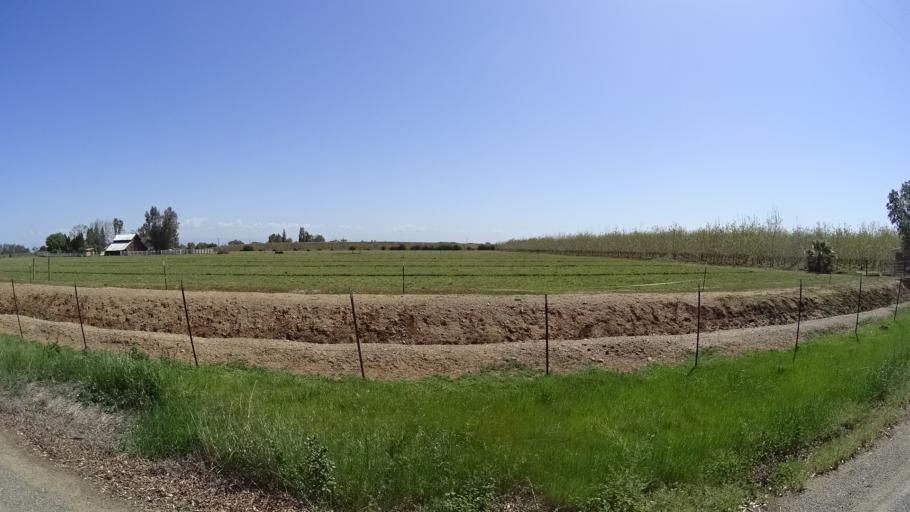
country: US
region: California
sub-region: Glenn County
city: Orland
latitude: 39.7959
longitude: -122.1594
